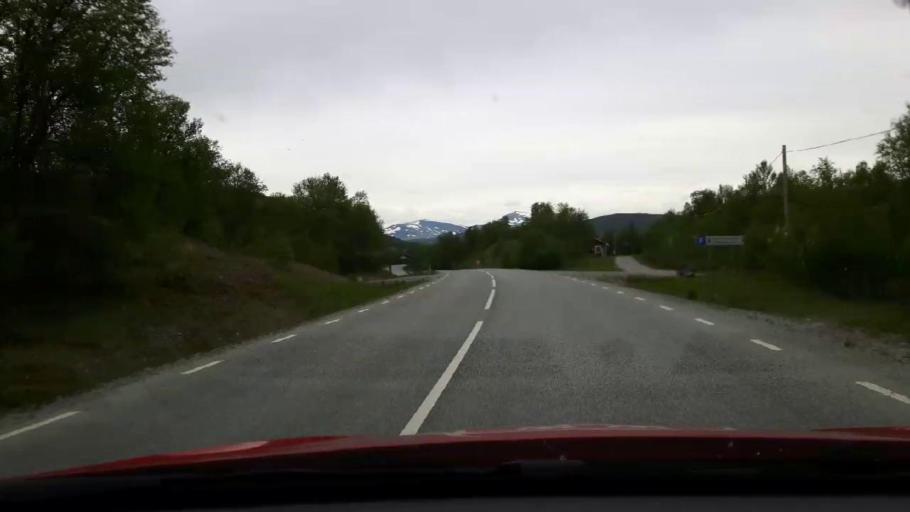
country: NO
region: Sor-Trondelag
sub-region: Tydal
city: Aas
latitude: 62.6939
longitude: 12.4063
